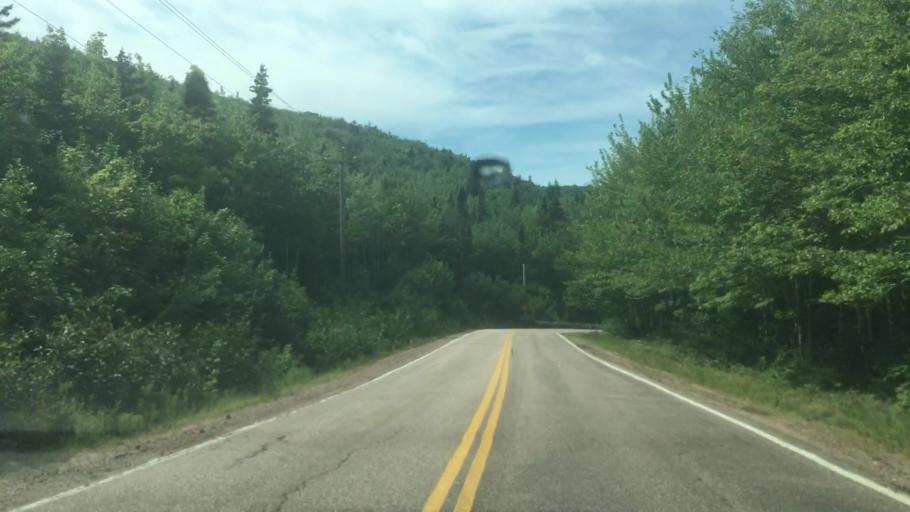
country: CA
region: Nova Scotia
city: Sydney Mines
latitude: 46.6061
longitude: -60.3959
